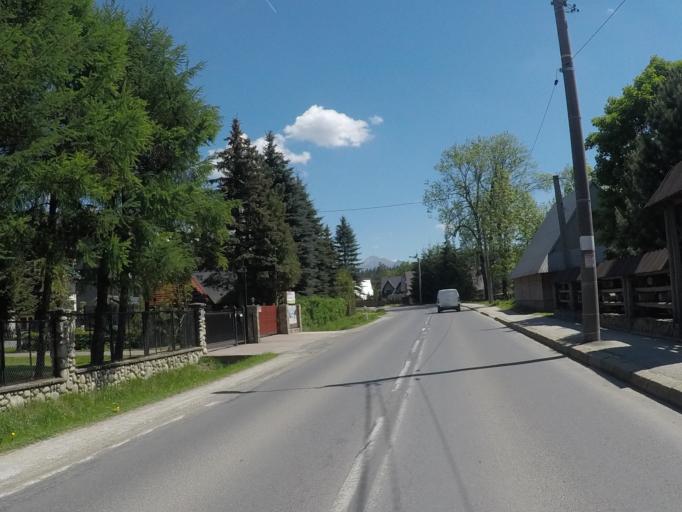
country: PL
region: Lesser Poland Voivodeship
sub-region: Powiat tatrzanski
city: Poronin
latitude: 49.3325
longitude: 20.0121
